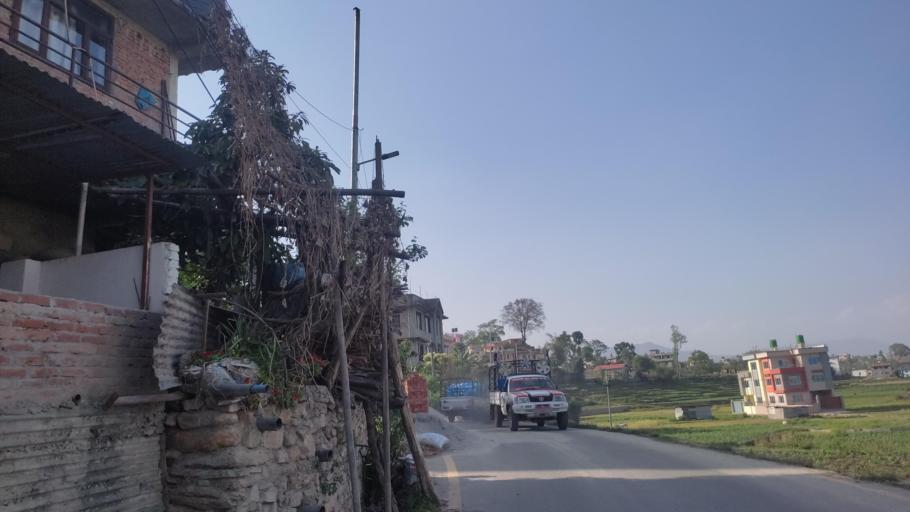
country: NP
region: Central Region
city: Kirtipur
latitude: 27.6511
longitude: 85.2772
